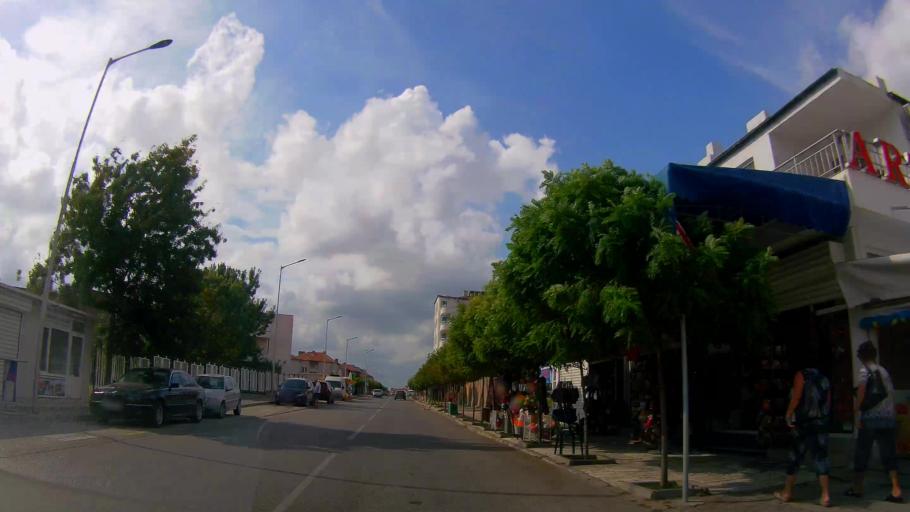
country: BG
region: Burgas
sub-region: Obshtina Primorsko
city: Primorsko
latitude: 42.2711
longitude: 27.7507
